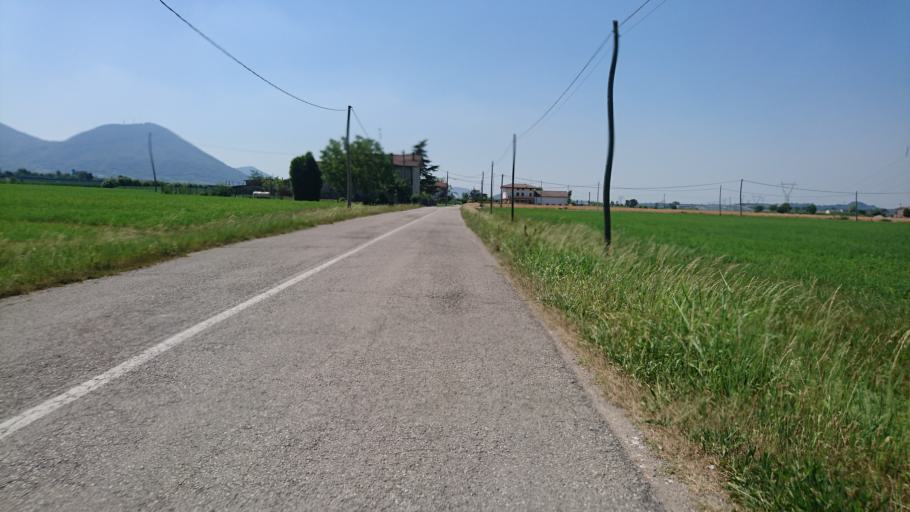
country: IT
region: Veneto
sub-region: Provincia di Padova
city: Bastia
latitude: 45.4018
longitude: 11.6238
